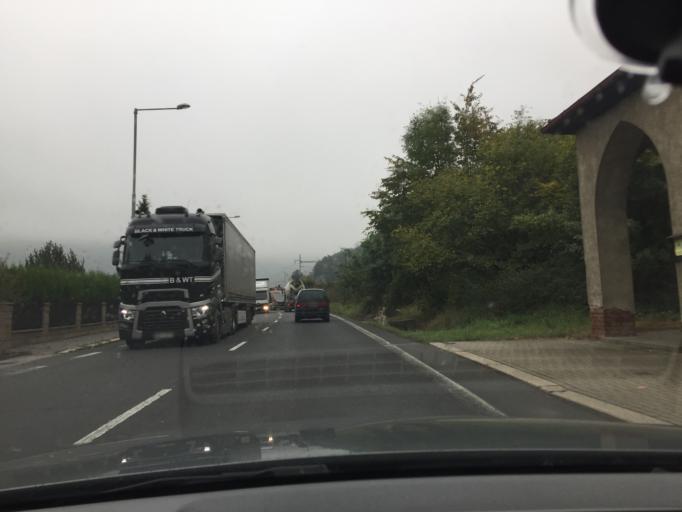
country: CZ
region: Ustecky
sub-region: Okres Usti nad Labem
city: Usti nad Labem
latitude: 50.6243
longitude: 14.0609
